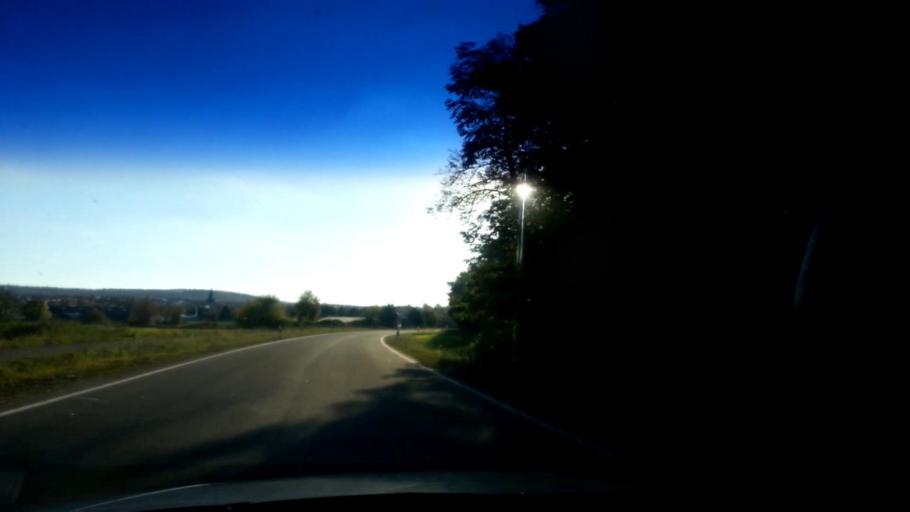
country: DE
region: Bavaria
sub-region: Upper Franconia
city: Baunach
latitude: 49.9925
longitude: 10.8597
